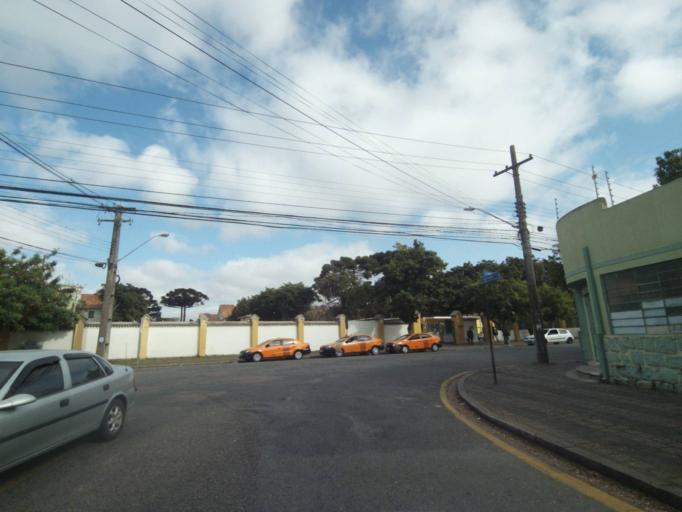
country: BR
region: Parana
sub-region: Curitiba
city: Curitiba
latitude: -25.4506
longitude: -49.2595
